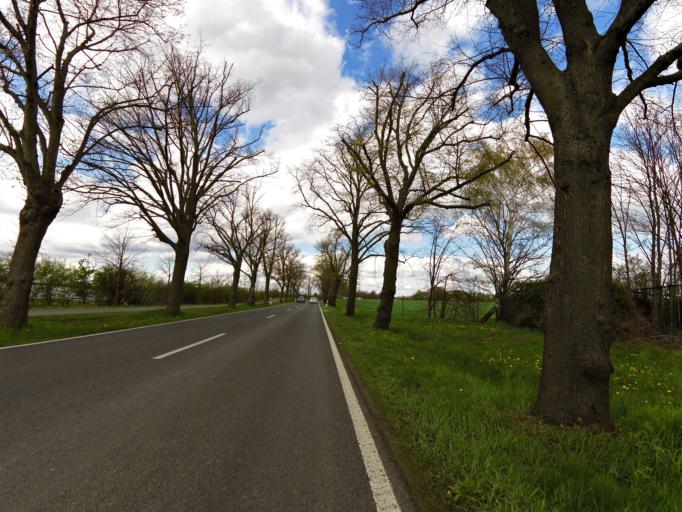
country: DE
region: Berlin
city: Lichtenrade
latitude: 52.3877
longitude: 13.4437
